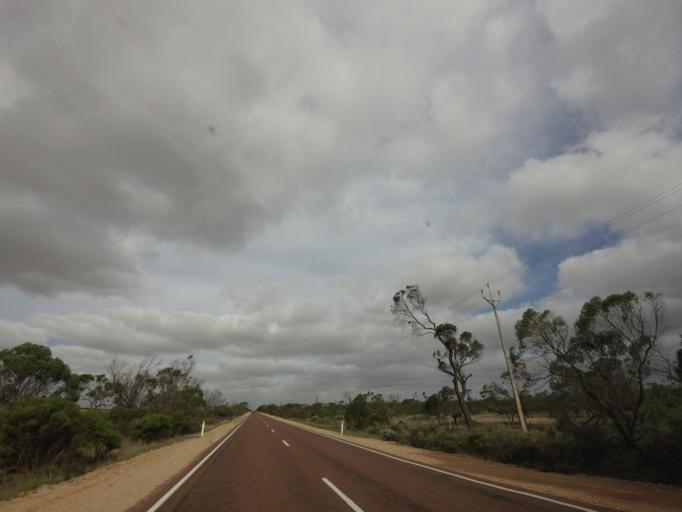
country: AU
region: South Australia
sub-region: Ceduna
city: Ceduna
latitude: -31.9409
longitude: 133.2378
